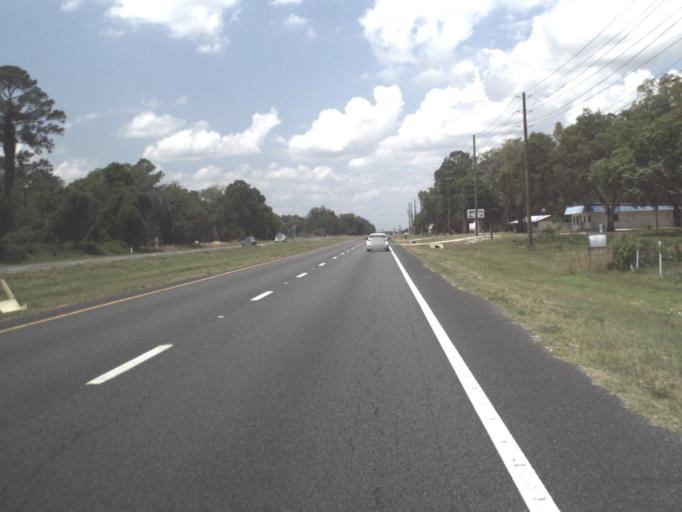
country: US
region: Florida
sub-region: Sumter County
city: Wildwood
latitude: 28.8368
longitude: -82.0085
